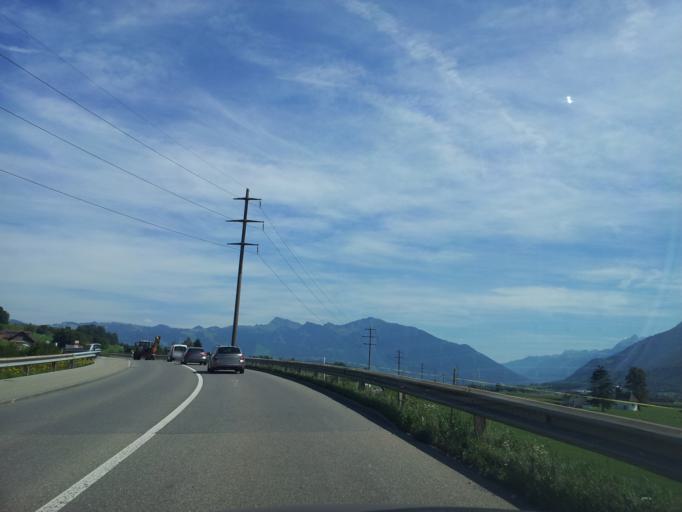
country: CH
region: Schwyz
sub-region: Bezirk March
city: Schubelbach
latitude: 47.1905
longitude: 8.9077
